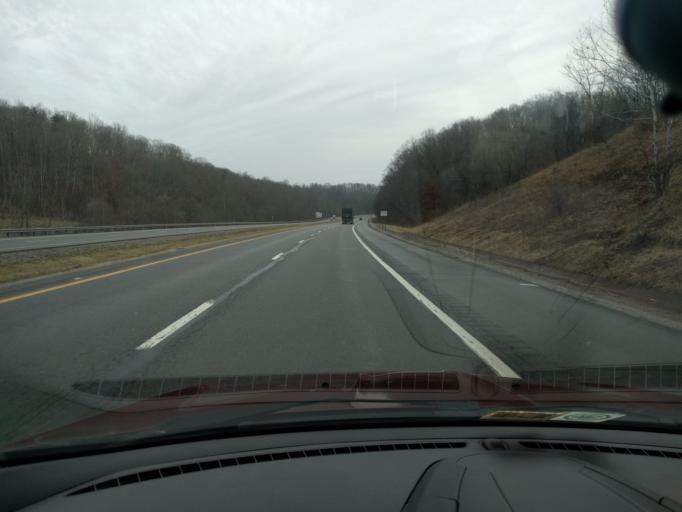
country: US
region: West Virginia
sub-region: Jackson County
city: Ravenswood
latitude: 39.0161
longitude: -81.6203
